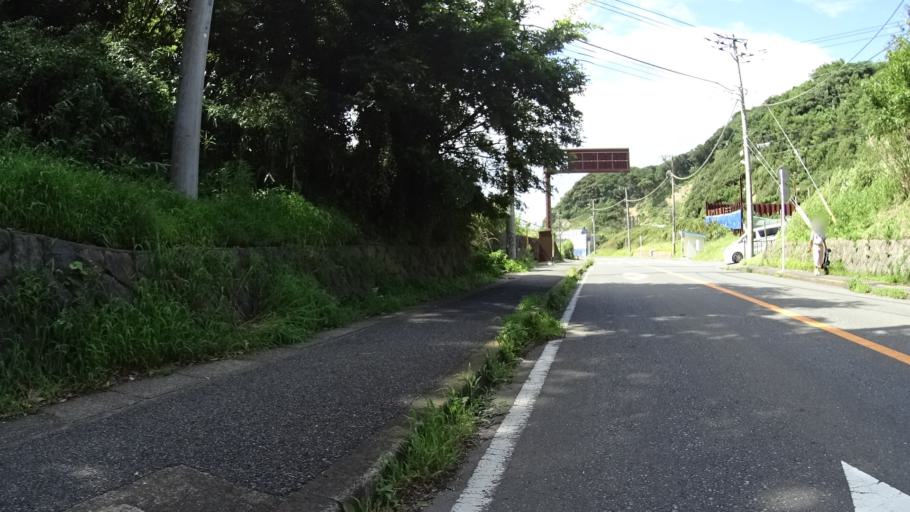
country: JP
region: Kanagawa
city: Yokosuka
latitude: 35.2135
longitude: 139.7112
